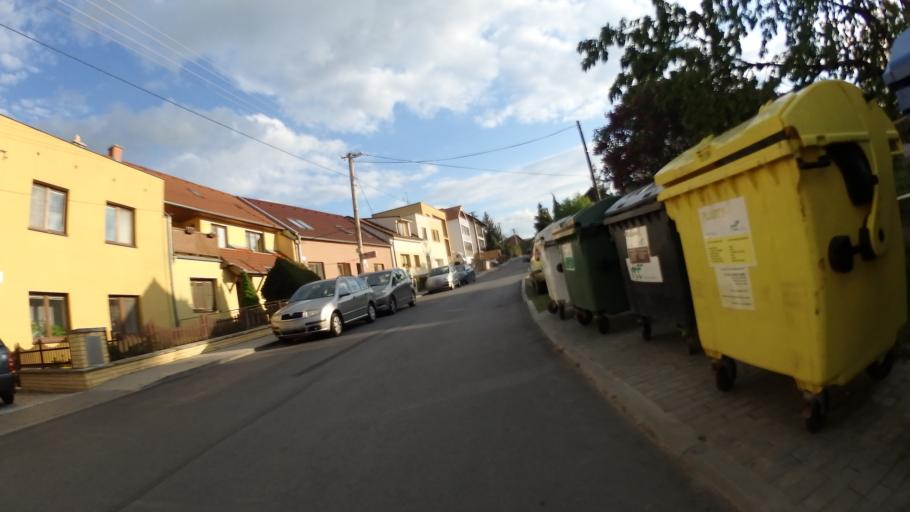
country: CZ
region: South Moravian
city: Moravany
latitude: 49.1452
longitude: 16.5793
